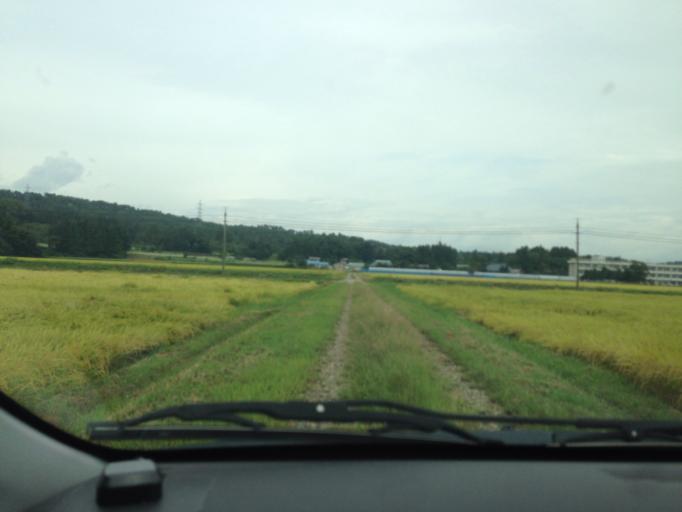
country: JP
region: Fukushima
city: Kitakata
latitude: 37.5846
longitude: 139.8080
